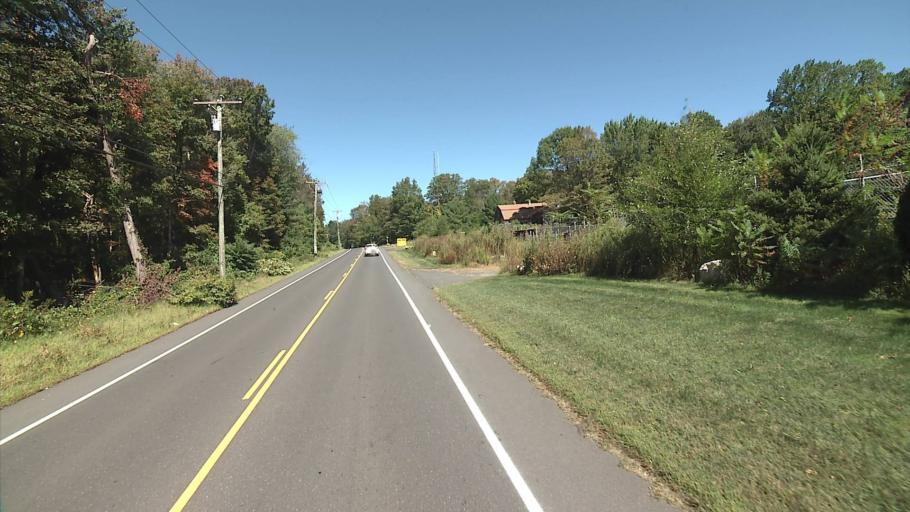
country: US
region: Connecticut
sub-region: New Haven County
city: Prospect
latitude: 41.4648
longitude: -72.9661
